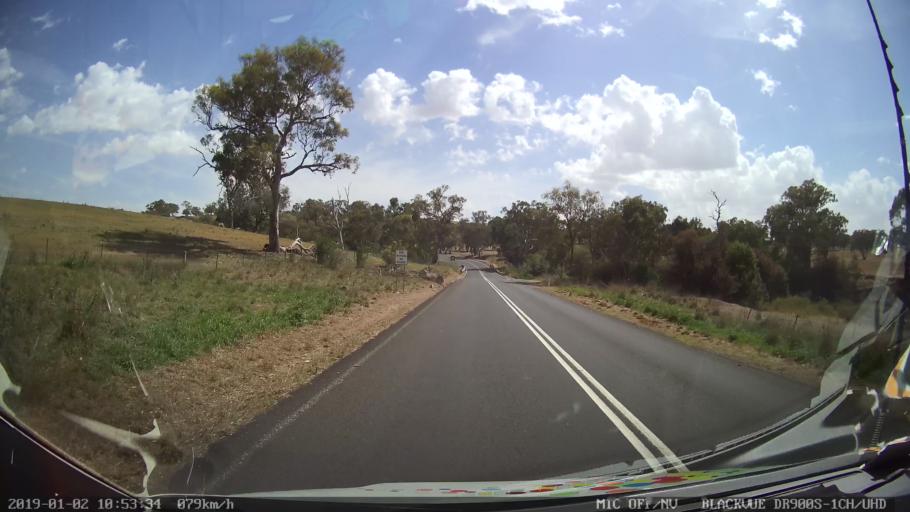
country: AU
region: New South Wales
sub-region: Cootamundra
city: Cootamundra
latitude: -34.6771
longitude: 148.2771
